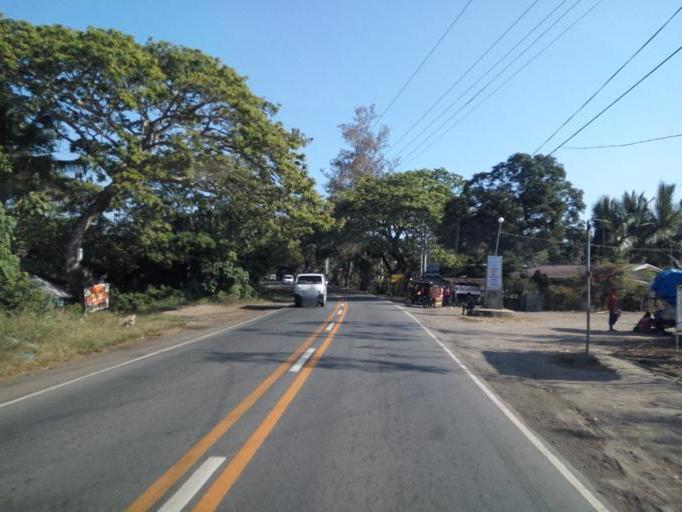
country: PH
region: Cagayan Valley
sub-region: Province of Cagayan
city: Amulung
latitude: 17.8236
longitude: 121.7258
